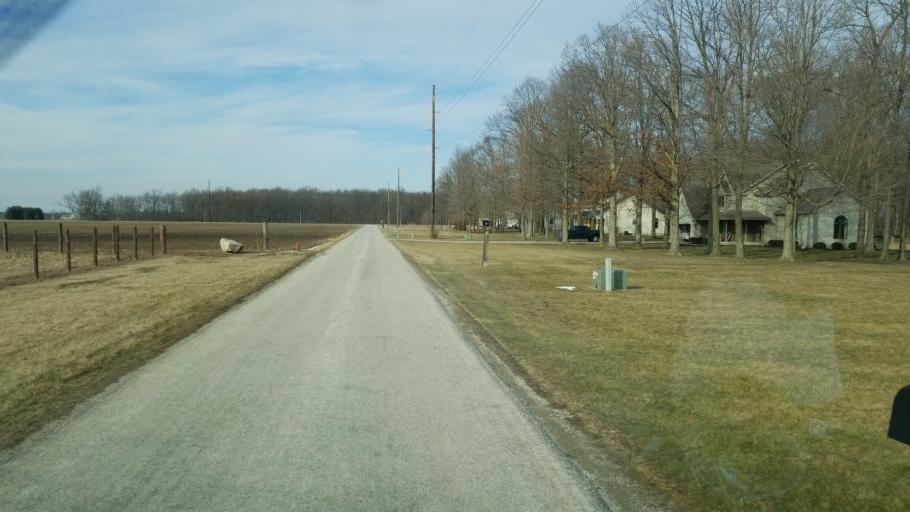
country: US
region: Ohio
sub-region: Marion County
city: Prospect
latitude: 40.4468
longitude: -83.2057
